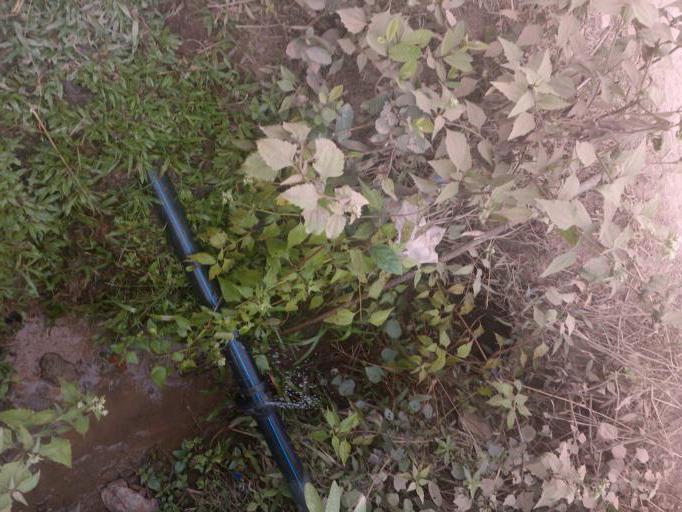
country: LA
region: Xiangkhoang
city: Muang Phonsavan
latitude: 19.3411
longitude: 103.5637
